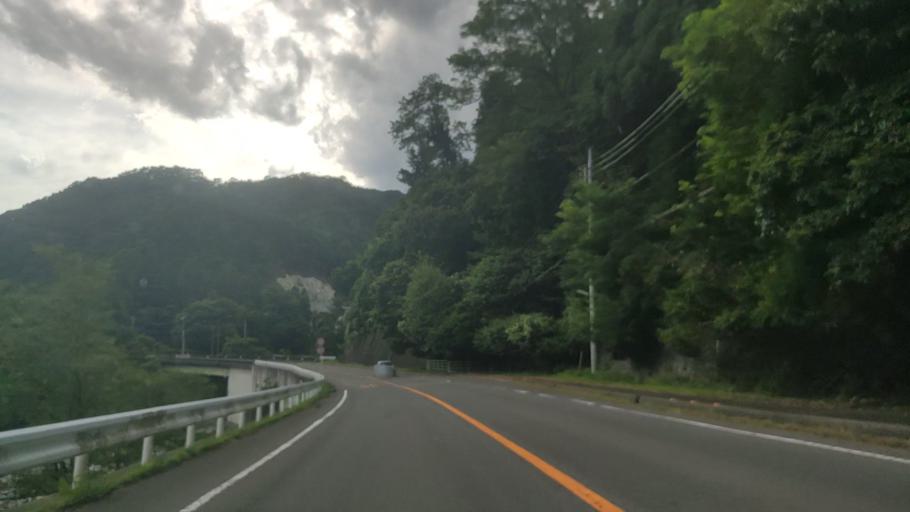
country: JP
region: Gunma
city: Omamacho-omama
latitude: 36.6156
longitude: 139.4120
